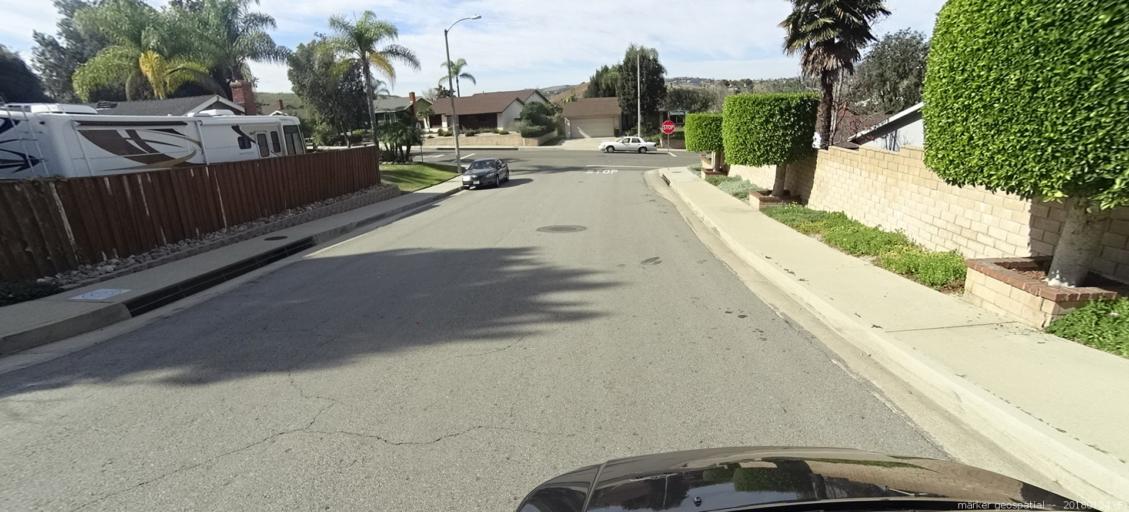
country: US
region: California
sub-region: Los Angeles County
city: Diamond Bar
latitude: 34.0286
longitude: -117.8167
